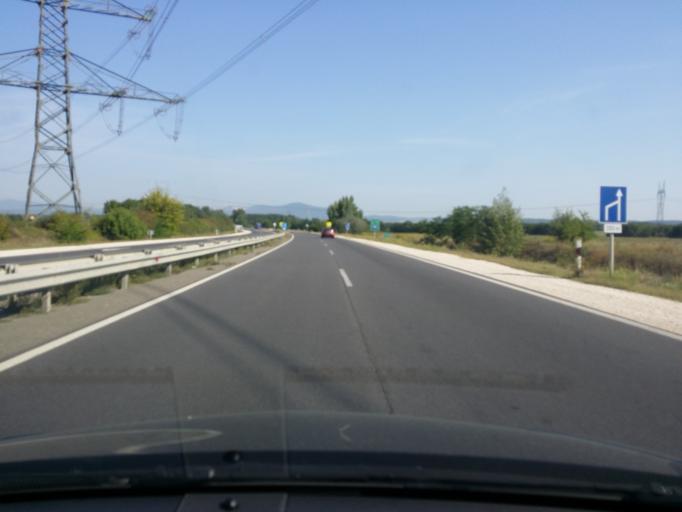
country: HU
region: Pest
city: Szod
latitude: 47.6865
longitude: 19.1749
